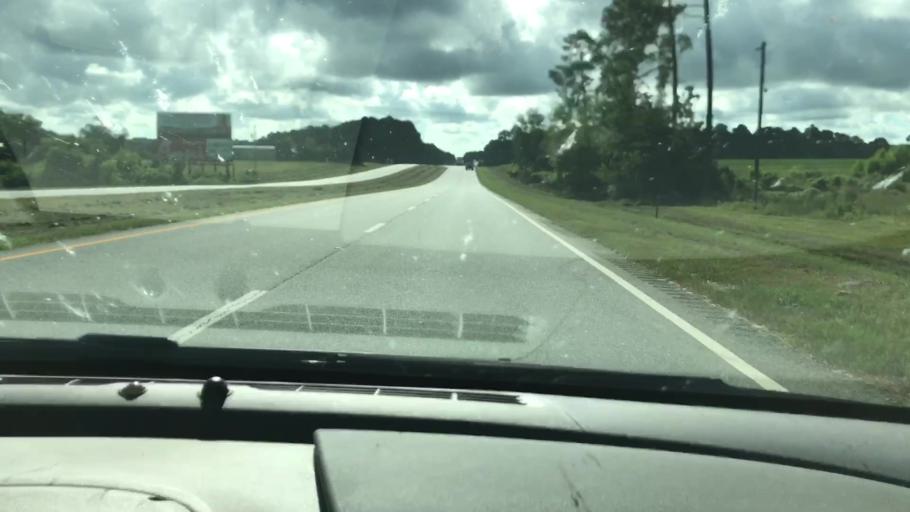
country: US
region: Georgia
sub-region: Tift County
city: Tifton
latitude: 31.4559
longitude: -83.6033
